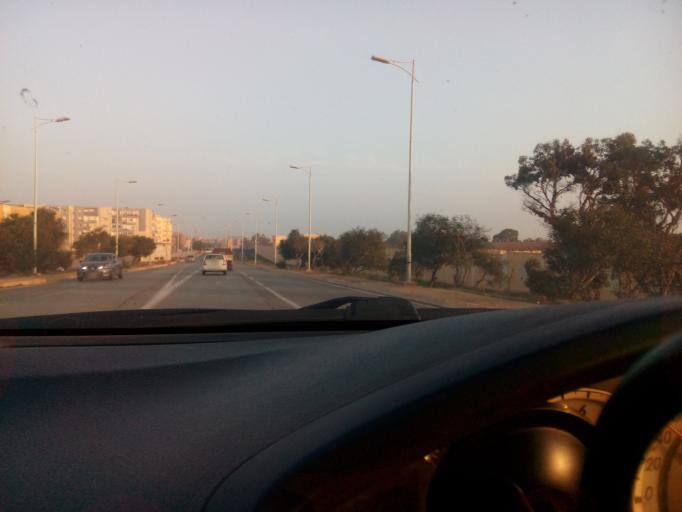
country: DZ
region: Oran
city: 'Ain el Turk
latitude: 35.7322
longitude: -0.7723
